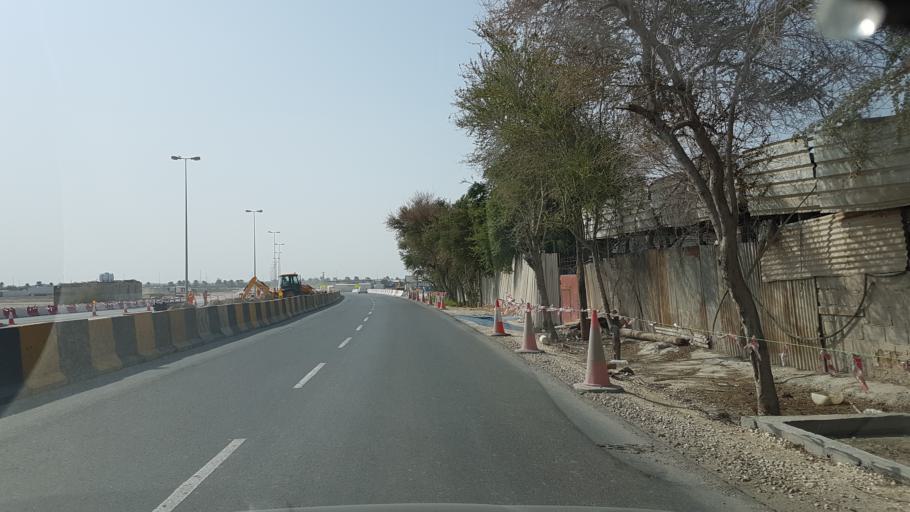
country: BH
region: Northern
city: Madinat `Isa
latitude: 26.1658
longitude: 50.5121
